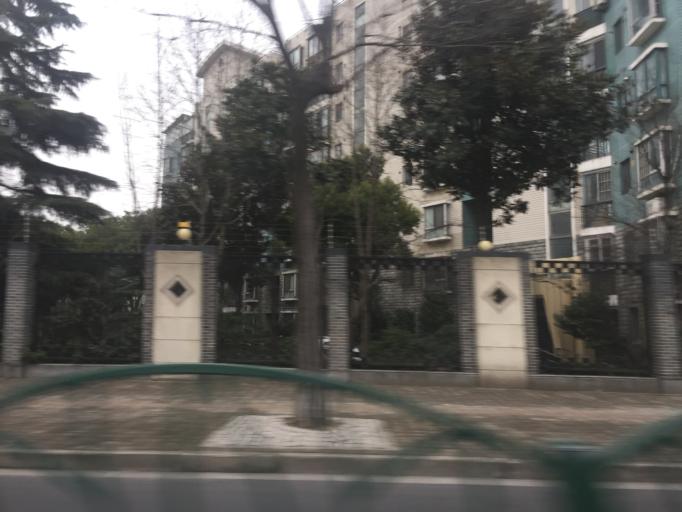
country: CN
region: Shanghai Shi
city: Luwan
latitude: 31.1866
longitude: 121.4945
